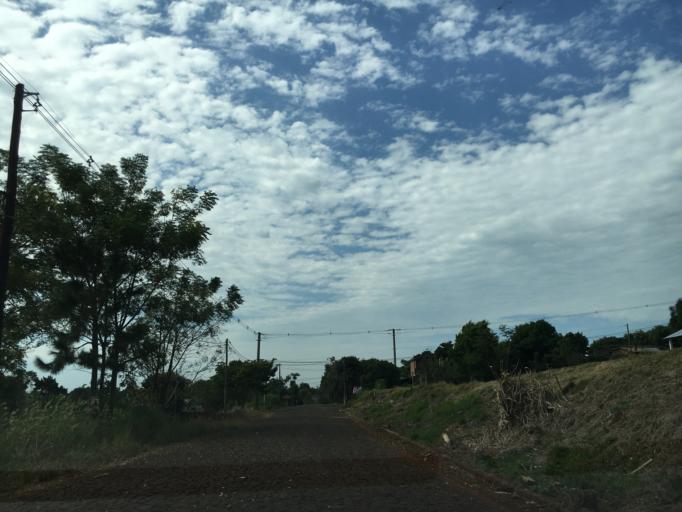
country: AR
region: Misiones
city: Puerto Rico
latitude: -26.7994
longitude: -55.0320
